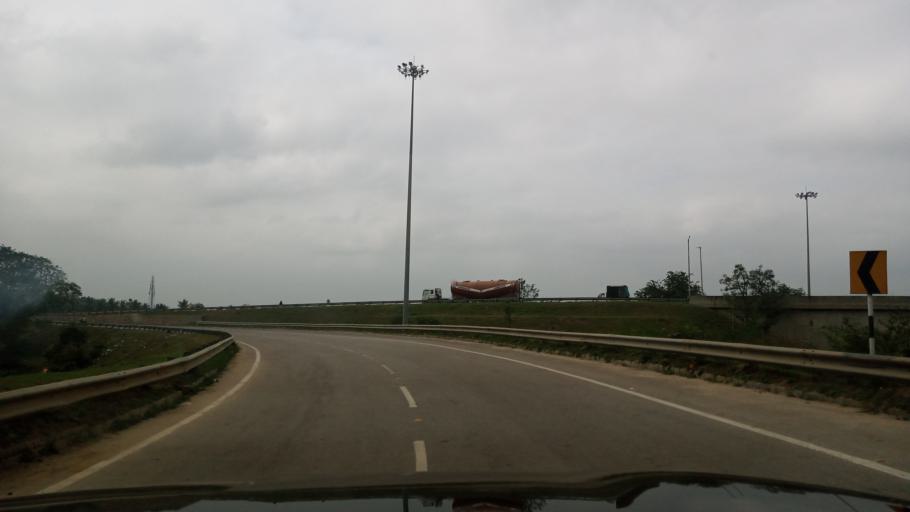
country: IN
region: Karnataka
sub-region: Bangalore Rural
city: Nelamangala
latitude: 13.0553
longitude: 77.4779
